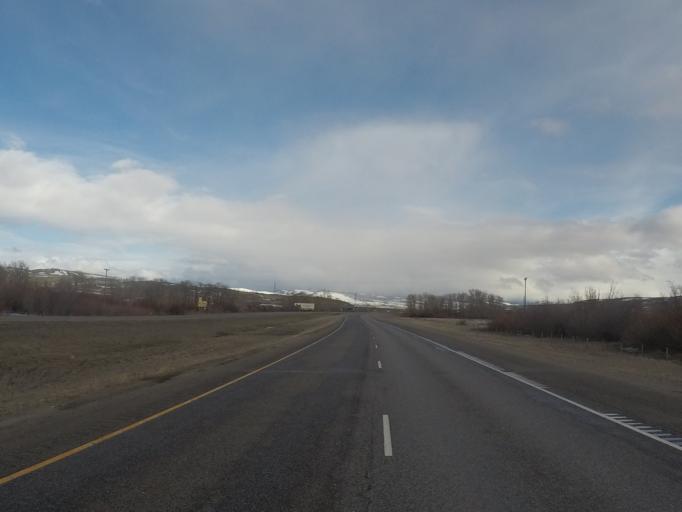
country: US
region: Montana
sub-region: Powell County
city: Deer Lodge
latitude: 46.5190
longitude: -112.8032
